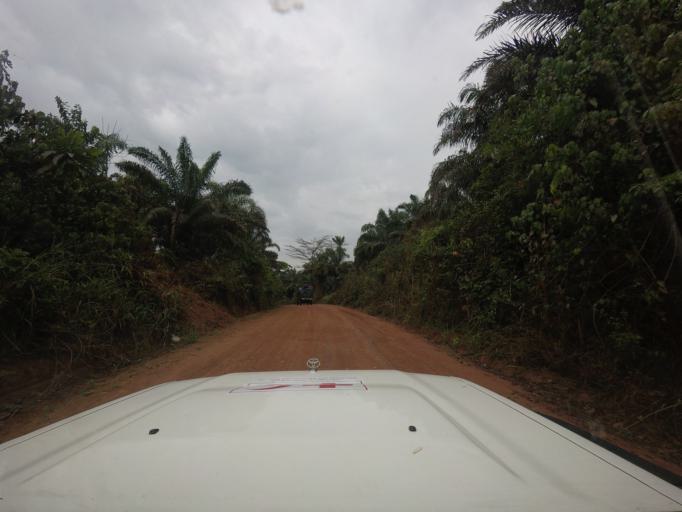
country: SL
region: Eastern Province
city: Buedu
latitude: 8.3115
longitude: -10.1395
